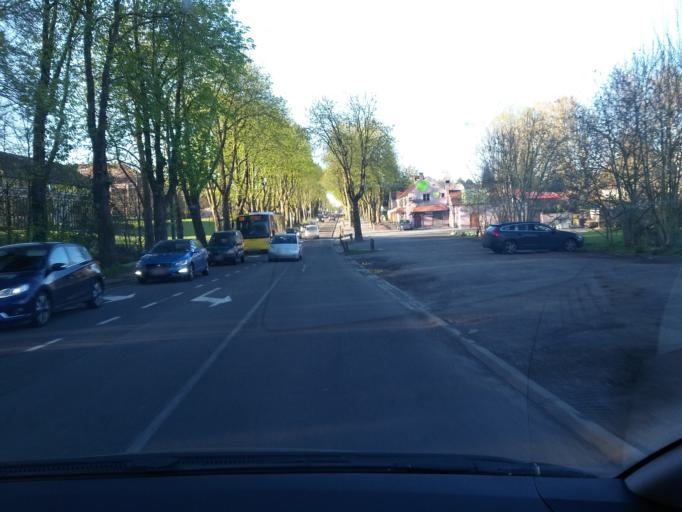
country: BE
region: Wallonia
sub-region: Province du Brabant Wallon
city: Waterloo
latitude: 50.7137
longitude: 4.4096
